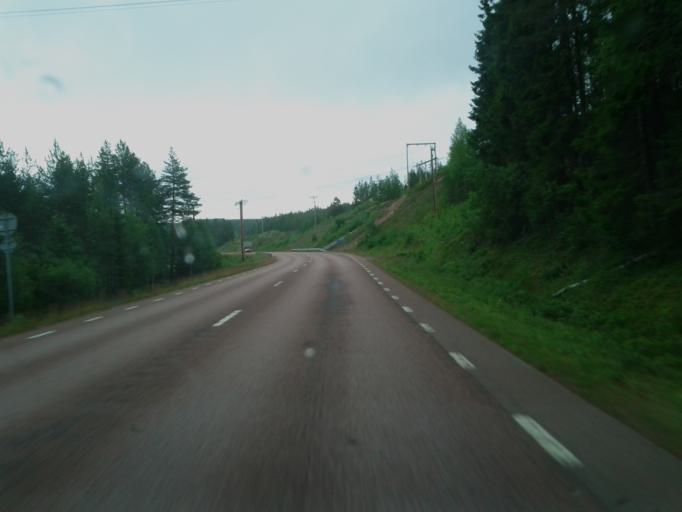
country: SE
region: Dalarna
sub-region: Alvdalens Kommun
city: AElvdalen
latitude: 61.2733
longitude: 13.7894
